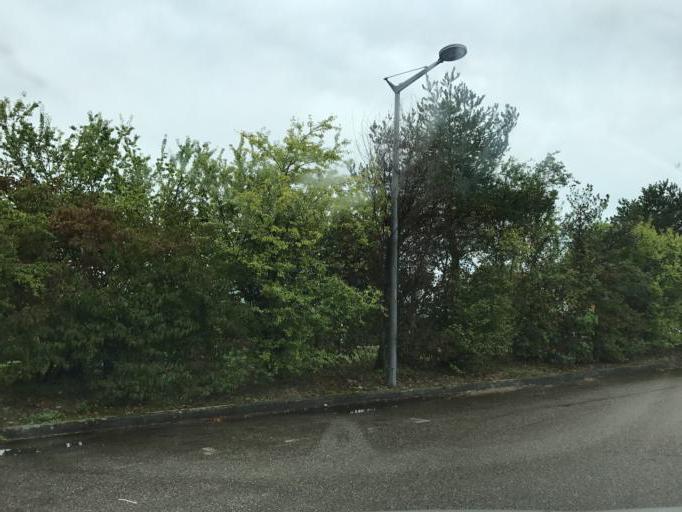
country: FR
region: Rhone-Alpes
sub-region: Departement du Rhone
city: Rillieux-la-Pape
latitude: 45.8121
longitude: 4.9047
